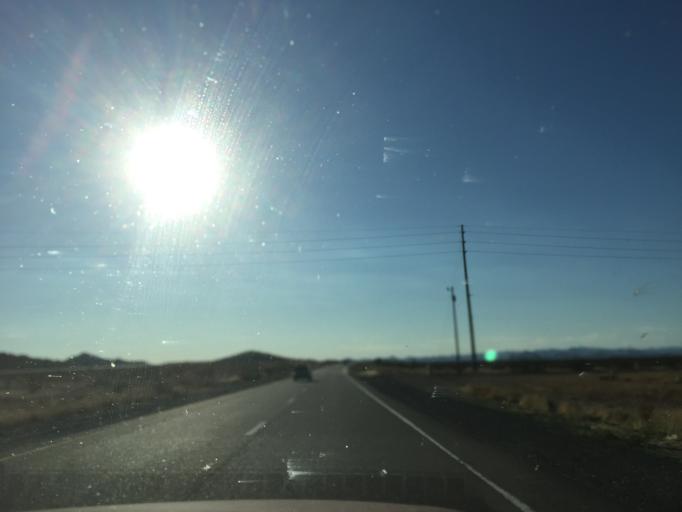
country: US
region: Arizona
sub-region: Maricopa County
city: Anthem
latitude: 33.7702
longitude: -112.1689
